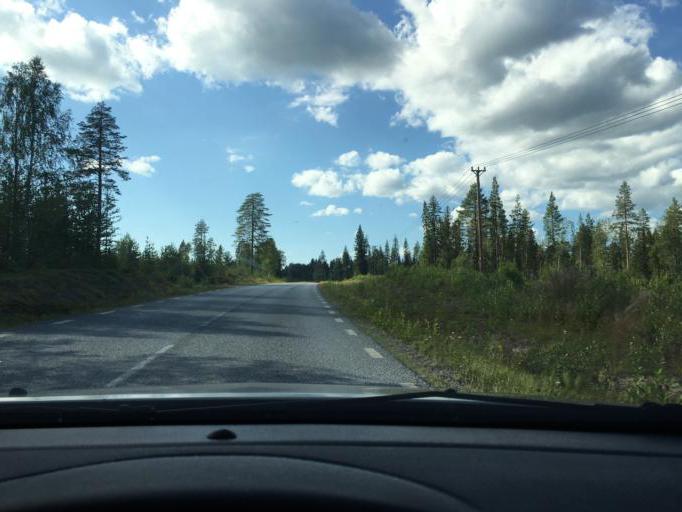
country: SE
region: Norrbotten
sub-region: Kalix Kommun
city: Toere
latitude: 66.0526
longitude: 22.5439
